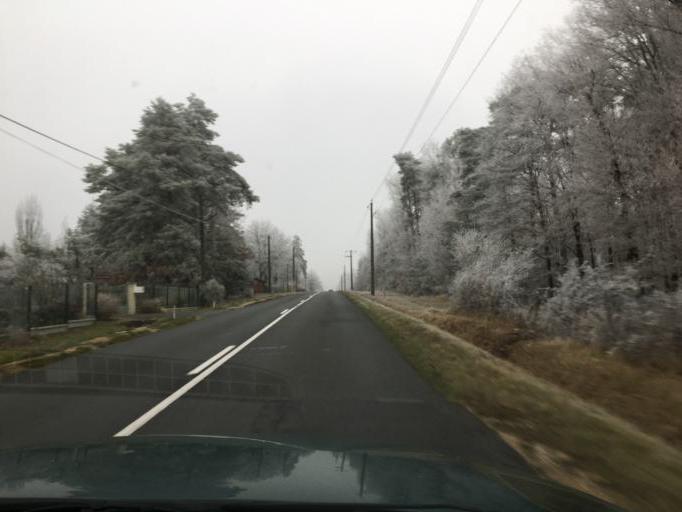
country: FR
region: Centre
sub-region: Departement du Loiret
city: Ligny-le-Ribault
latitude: 47.6957
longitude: 1.7879
